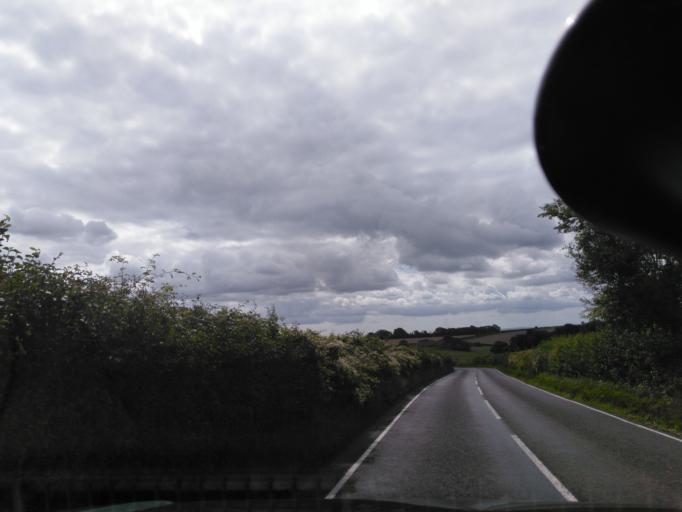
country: GB
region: England
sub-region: Dorset
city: Blandford Forum
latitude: 50.9056
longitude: -2.1580
